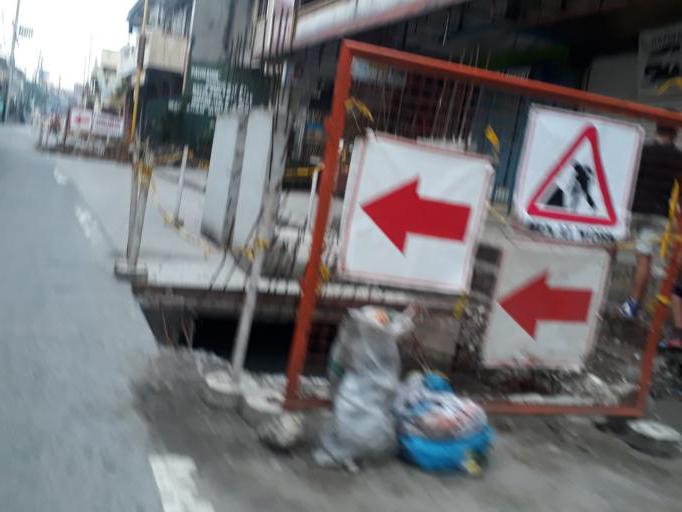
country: PH
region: Calabarzon
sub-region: Province of Rizal
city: Malabon
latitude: 14.6715
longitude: 120.9391
